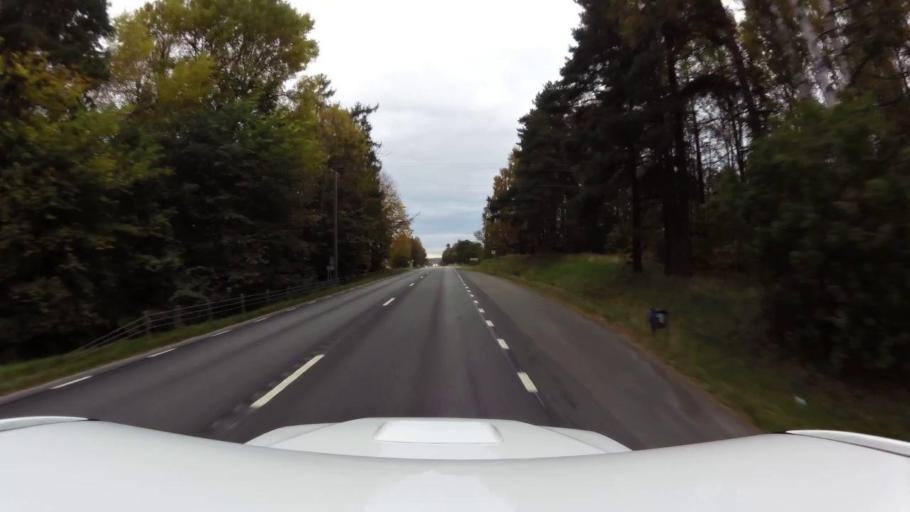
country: SE
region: OEstergoetland
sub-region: Linkopings Kommun
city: Ljungsbro
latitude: 58.5065
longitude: 15.4502
